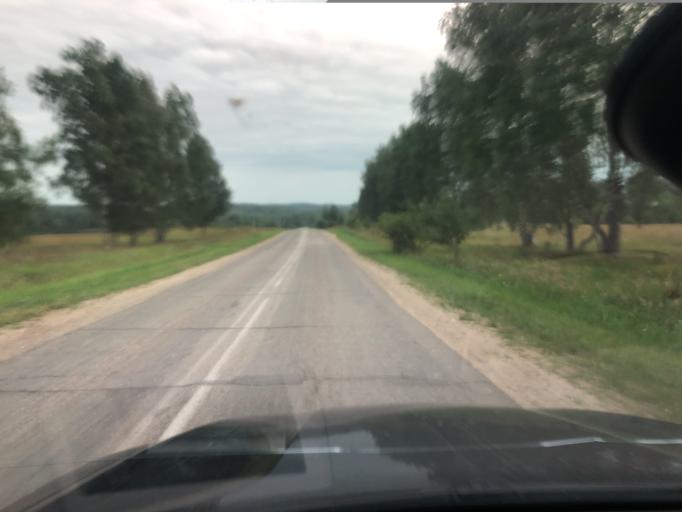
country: RU
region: Jaroslavl
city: Petrovsk
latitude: 56.9858
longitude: 39.1261
